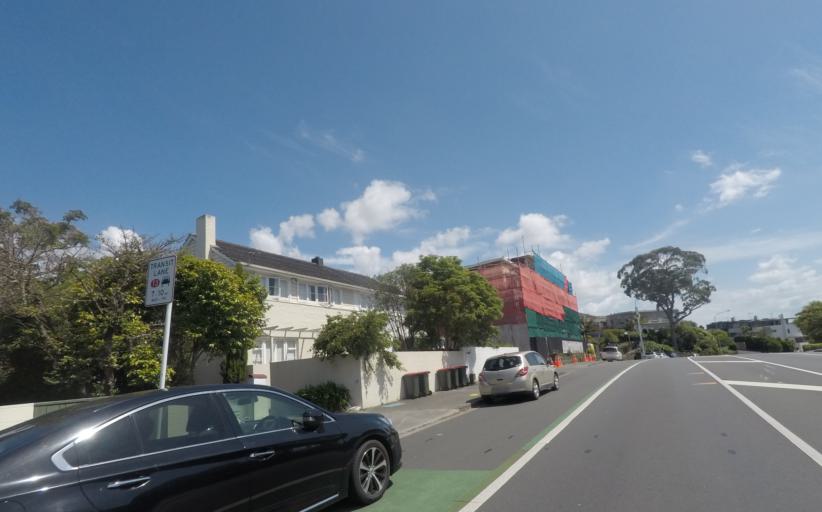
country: NZ
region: Auckland
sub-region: Auckland
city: Tamaki
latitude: -36.8790
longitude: 174.8224
